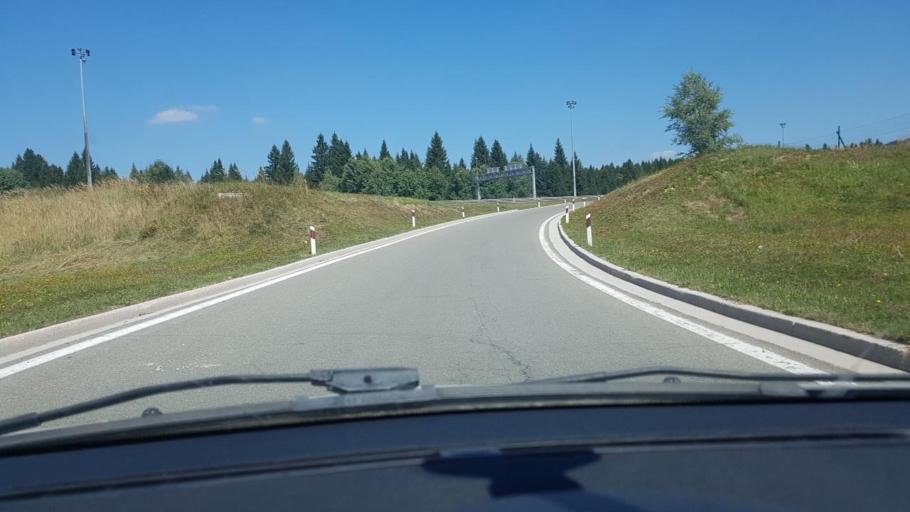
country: HR
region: Primorsko-Goranska
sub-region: Grad Delnice
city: Delnice
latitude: 45.3833
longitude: 14.9134
